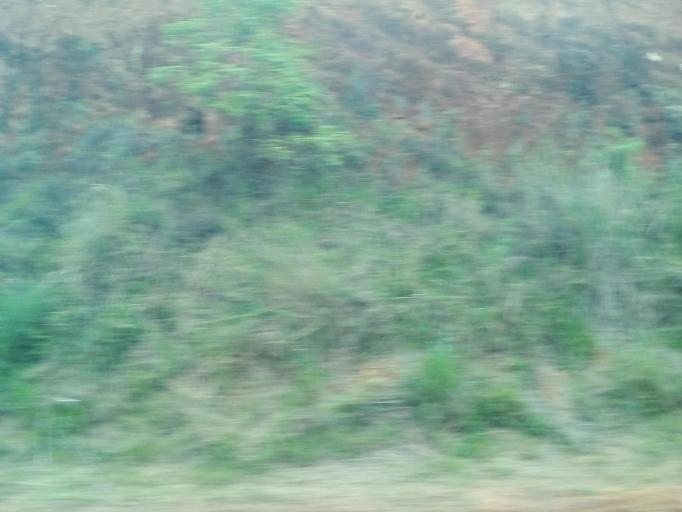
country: BR
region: Minas Gerais
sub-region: Nova Era
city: Nova Era
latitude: -19.7499
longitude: -43.0229
